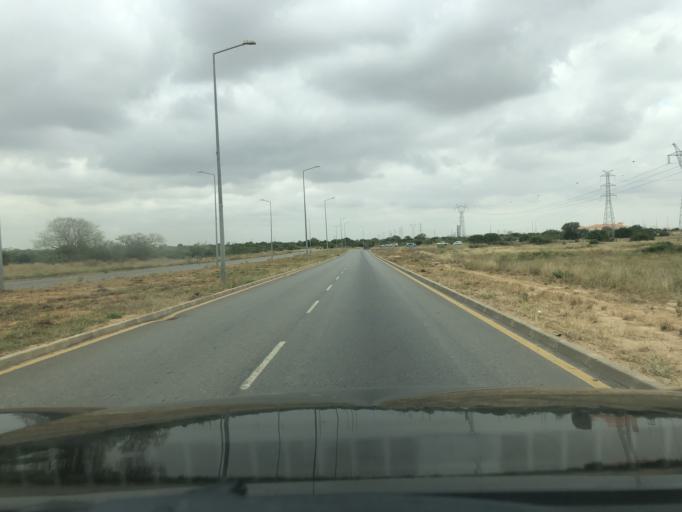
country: AO
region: Luanda
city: Luanda
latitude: -8.9757
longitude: 13.2796
